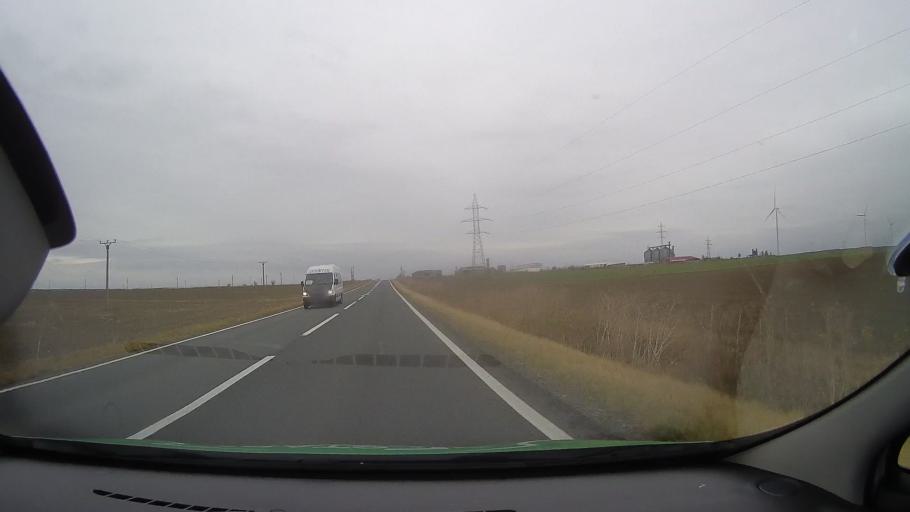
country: RO
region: Constanta
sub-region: Comuna Nicolae Balcescu
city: Dorobantu
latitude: 44.4250
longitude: 28.3093
